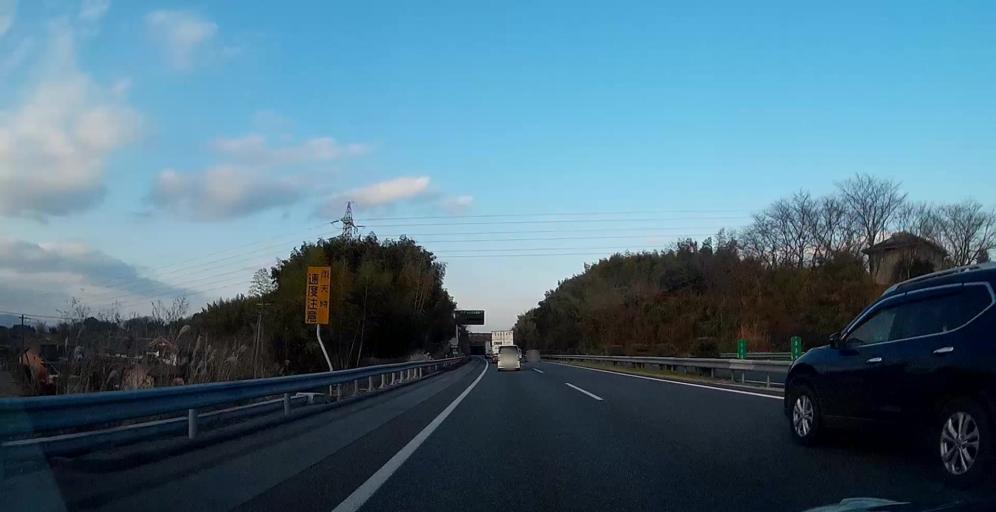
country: JP
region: Kumamoto
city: Uto
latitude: 32.6857
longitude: 130.7351
